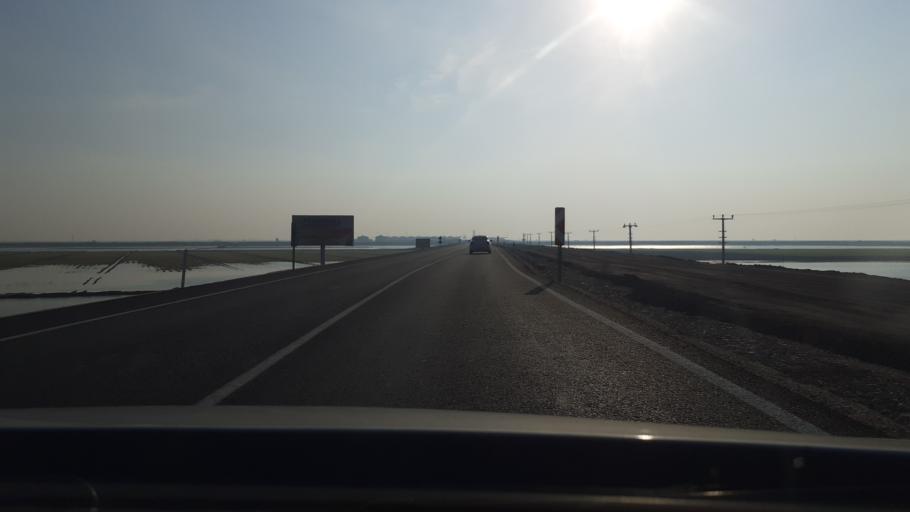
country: TR
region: Hatay
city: Serinyol
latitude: 36.3683
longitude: 36.2604
